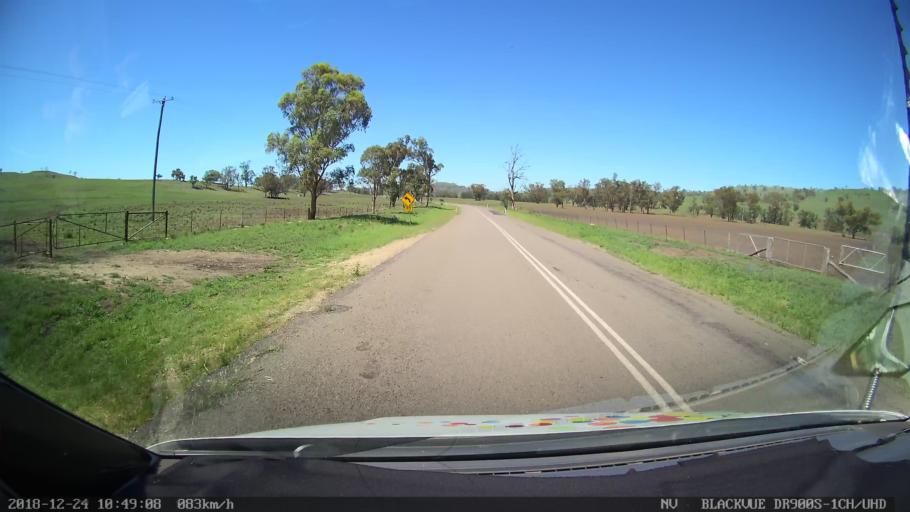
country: AU
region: New South Wales
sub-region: Upper Hunter Shire
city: Merriwa
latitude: -31.9439
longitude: 150.4290
